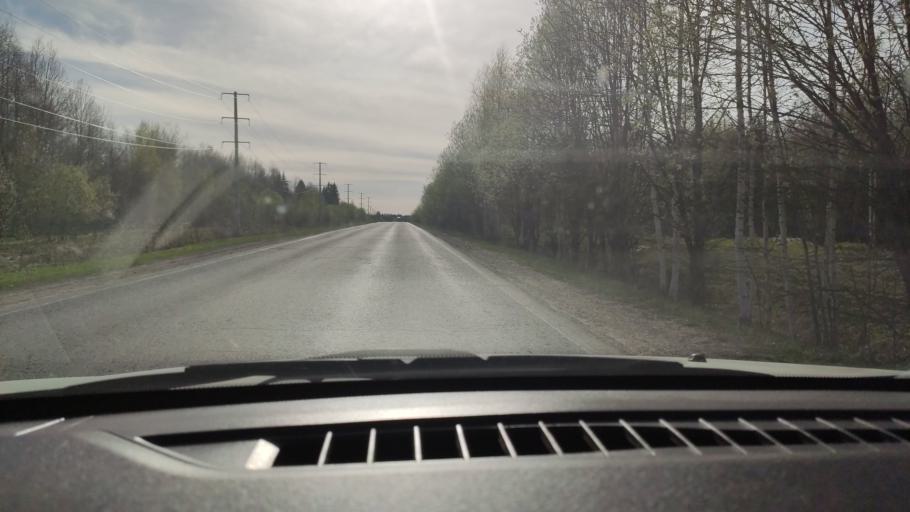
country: RU
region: Perm
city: Novyye Lyady
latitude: 57.9391
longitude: 56.5883
